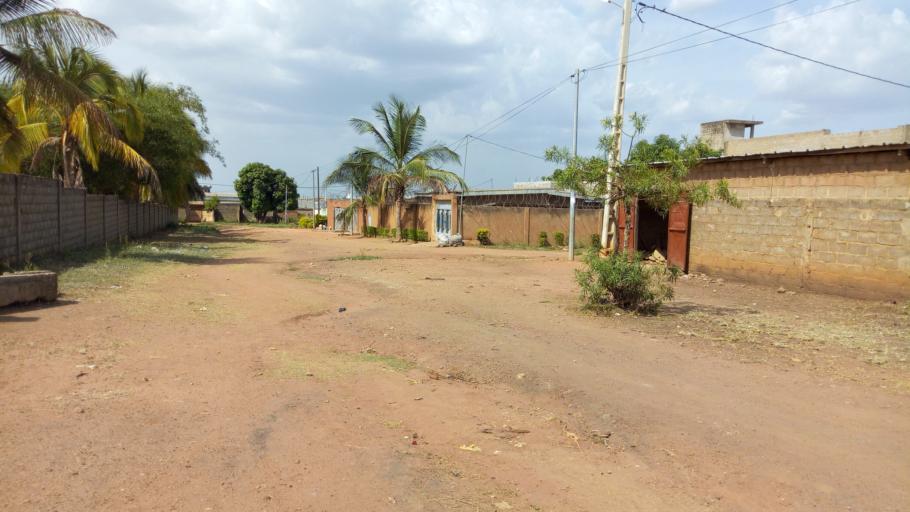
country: CI
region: Vallee du Bandama
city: Bouake
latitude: 7.7108
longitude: -5.0440
